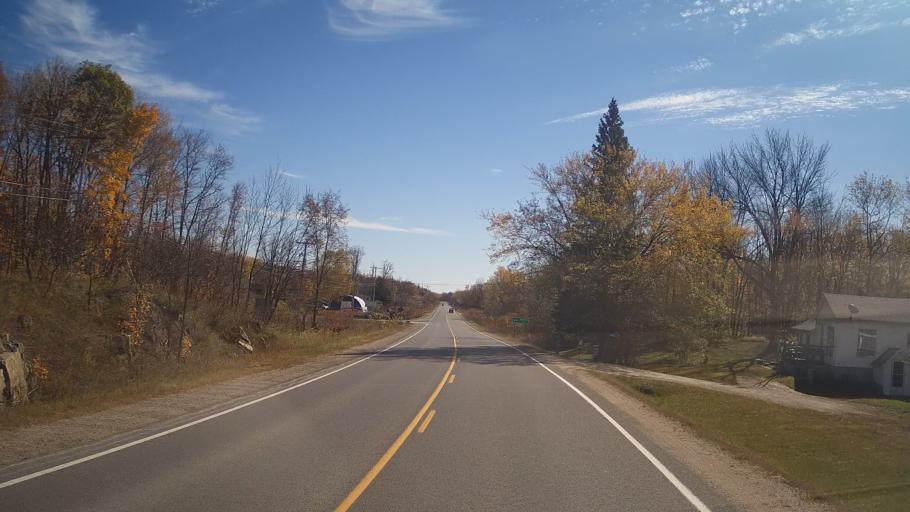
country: CA
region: Ontario
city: Perth
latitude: 44.7475
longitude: -76.6888
